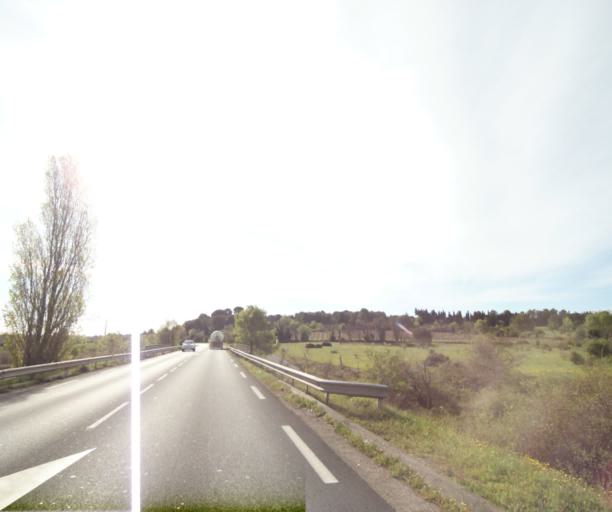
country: FR
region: Languedoc-Roussillon
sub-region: Departement de l'Herault
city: Saint-Jean-de-Vedas
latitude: 43.5870
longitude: 3.8354
